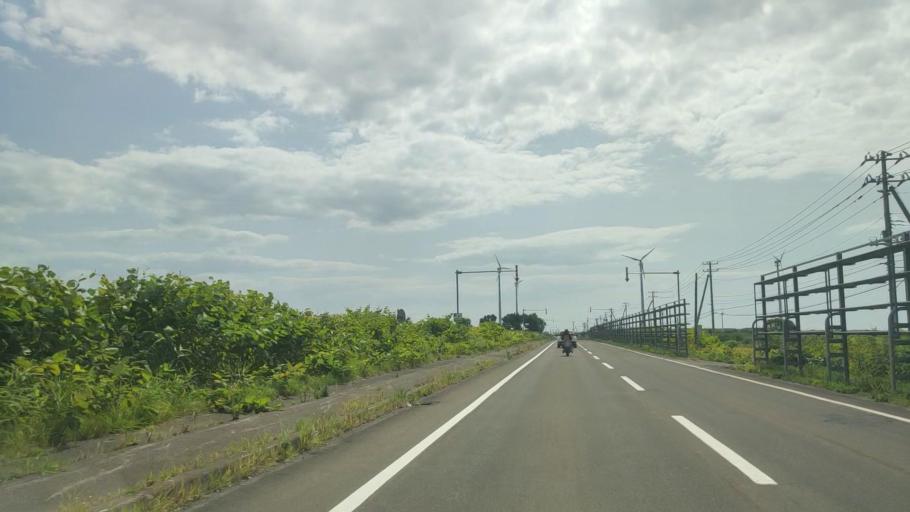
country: JP
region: Hokkaido
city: Rumoi
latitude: 44.3929
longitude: 141.7174
